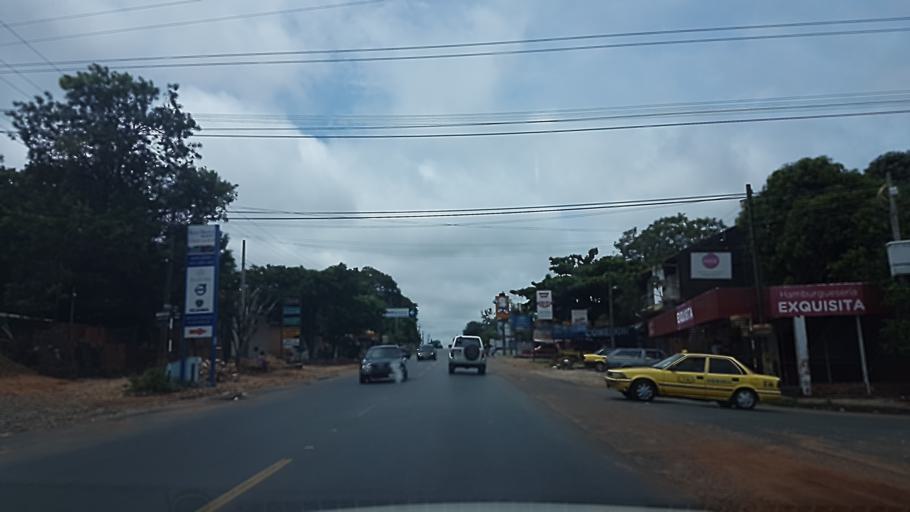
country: PY
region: Central
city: Lambare
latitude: -25.3516
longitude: -57.5920
